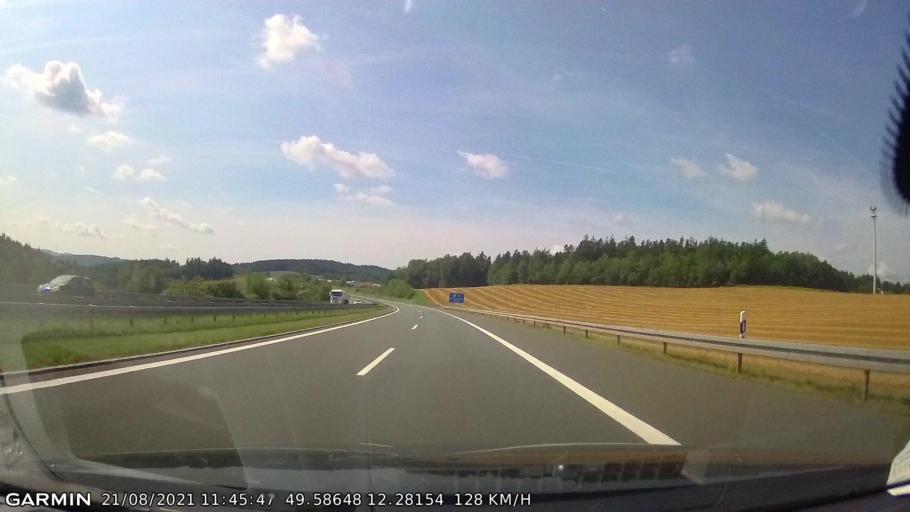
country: DE
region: Bavaria
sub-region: Upper Palatinate
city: Leuchtenberg
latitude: 49.5864
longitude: 12.2812
